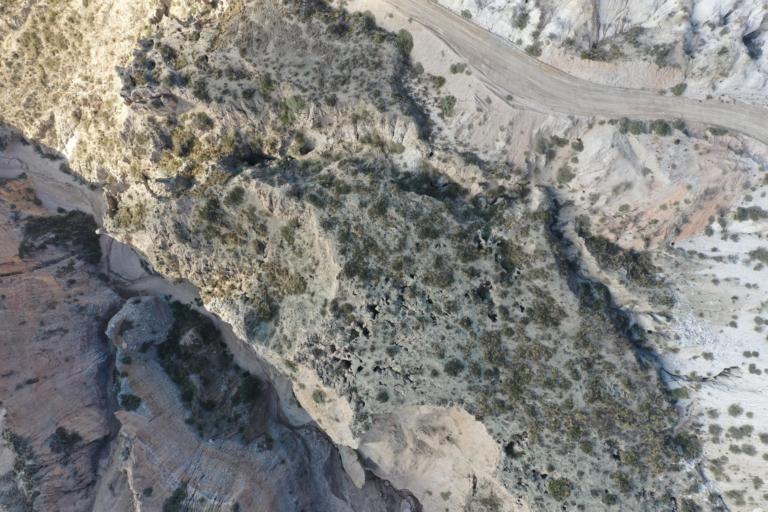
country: BO
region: La Paz
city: La Paz
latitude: -16.5595
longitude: -68.1309
